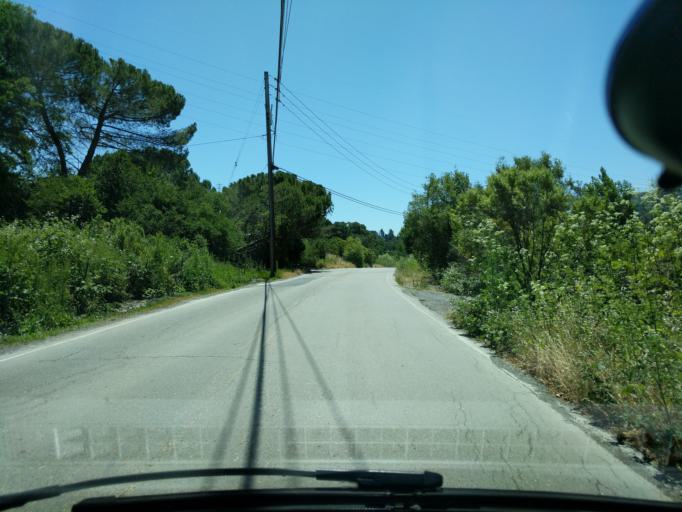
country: US
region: California
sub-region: Contra Costa County
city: Orinda
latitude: 37.9038
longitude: -122.2081
